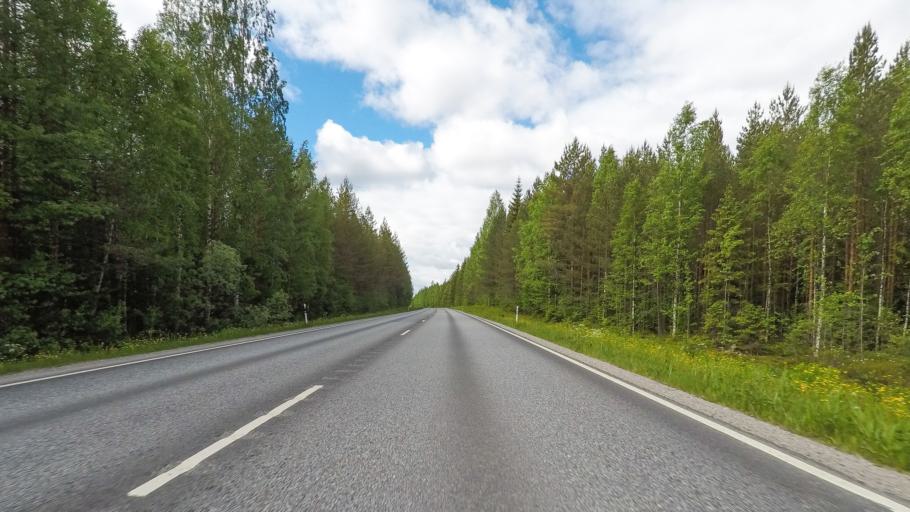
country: FI
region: Central Finland
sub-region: Jyvaeskylae
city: Toivakka
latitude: 62.2251
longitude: 26.2003
